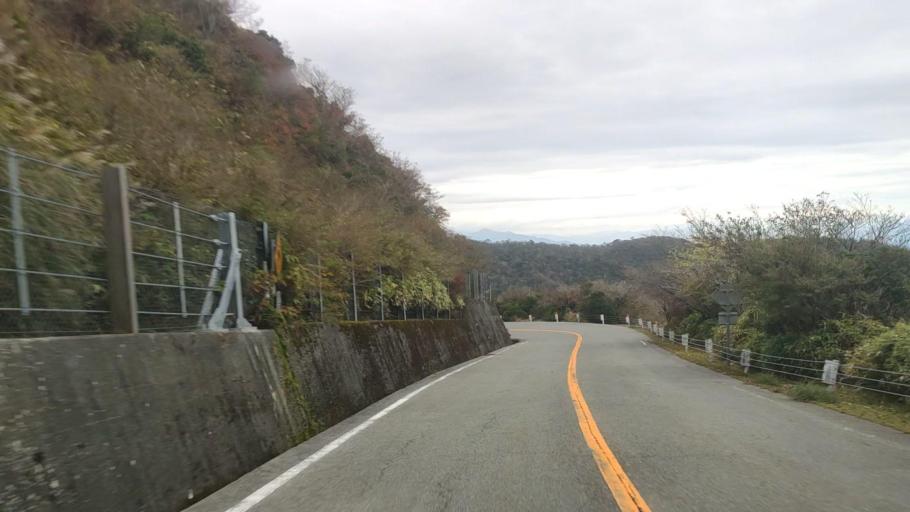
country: JP
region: Shizuoka
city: Heda
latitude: 34.9575
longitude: 138.8399
